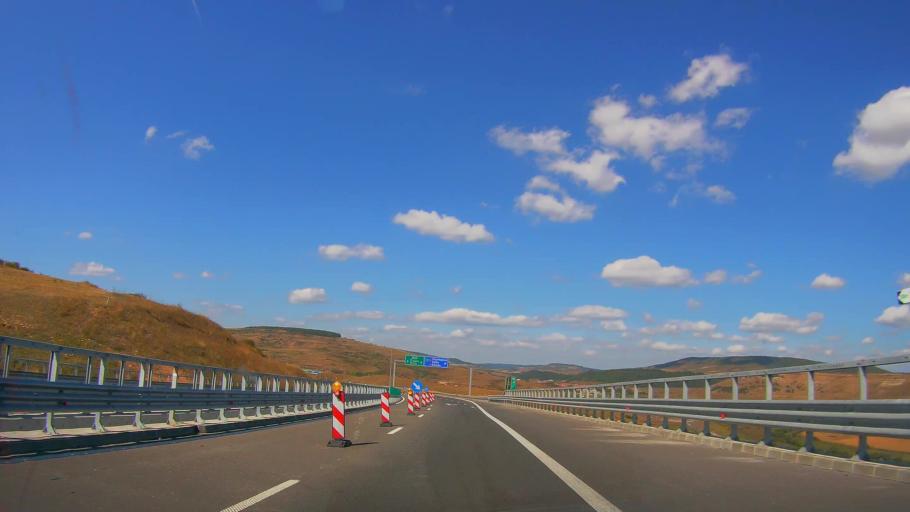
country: RO
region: Cluj
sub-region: Comuna Baciu
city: Mera
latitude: 46.8034
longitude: 23.4268
